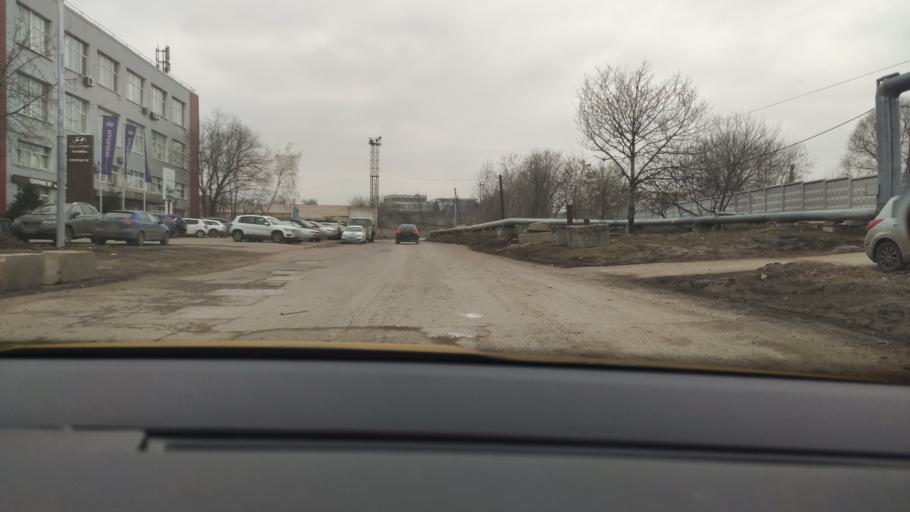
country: RU
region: Moscow
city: Tsaritsyno
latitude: 55.6097
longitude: 37.6321
